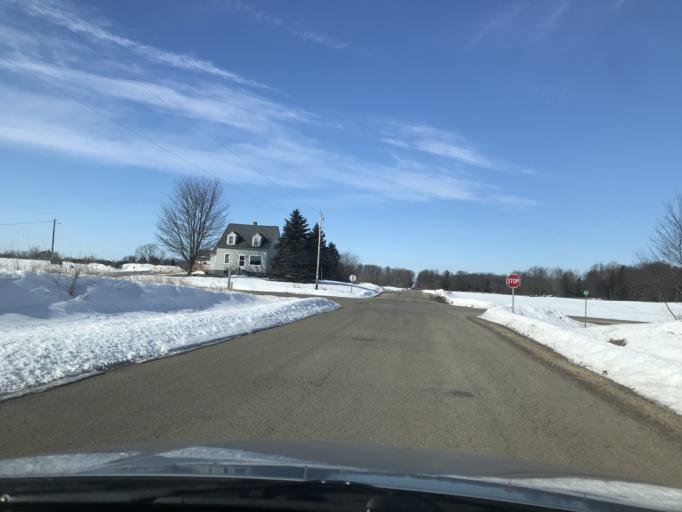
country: US
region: Wisconsin
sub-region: Oconto County
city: Oconto Falls
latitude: 44.9389
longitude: -88.2149
